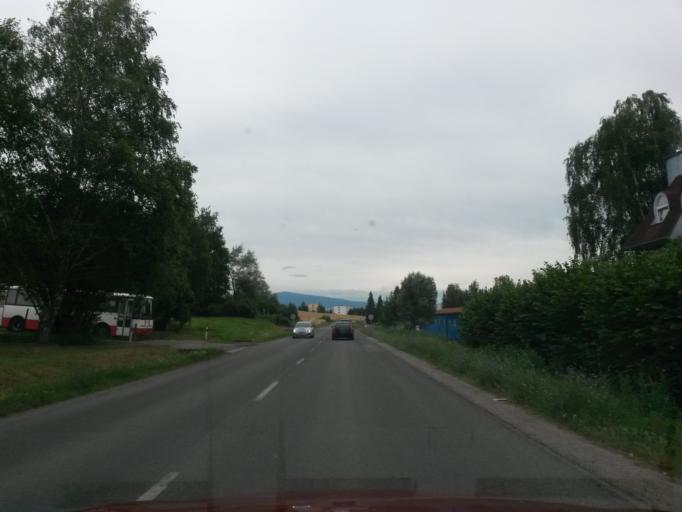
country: SK
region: Banskobystricky
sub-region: Okres Banska Bystrica
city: Zvolen
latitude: 48.5766
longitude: 19.1749
